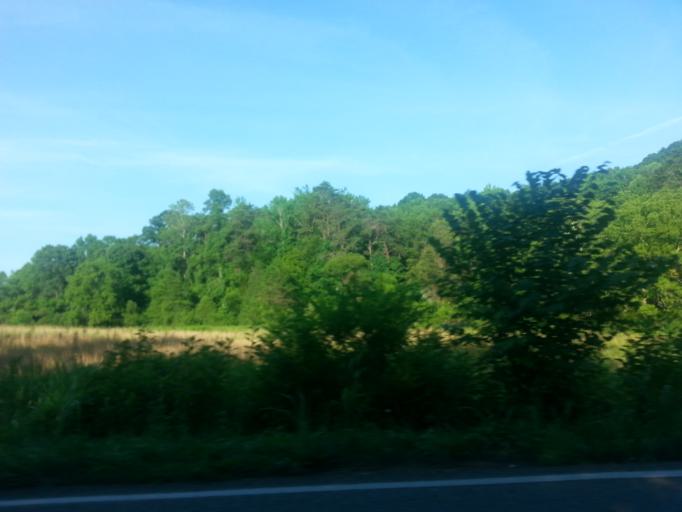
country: US
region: Tennessee
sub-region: Blount County
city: Maryville
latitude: 35.6767
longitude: -83.9741
